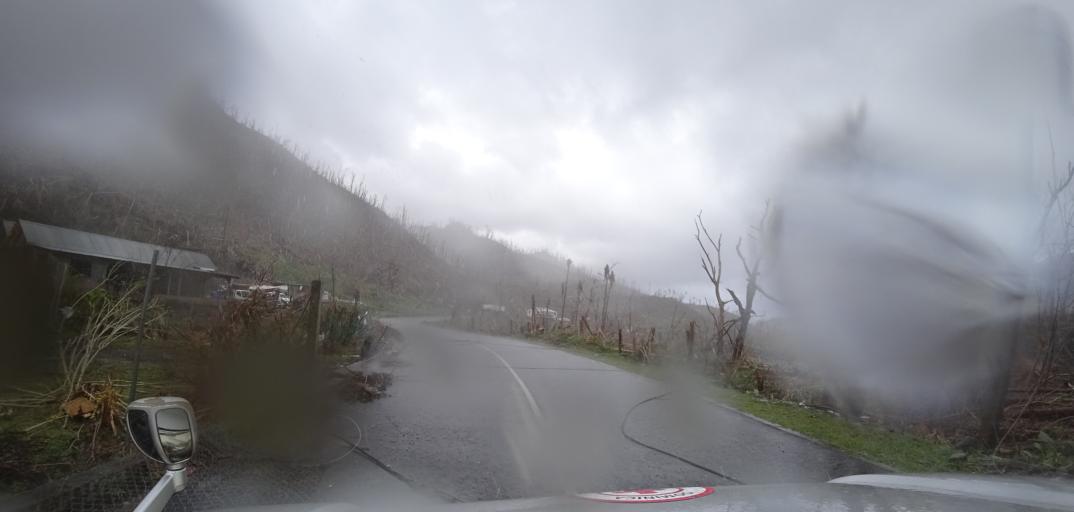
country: DM
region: Saint Andrew
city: Marigot
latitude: 15.4883
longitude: -61.2773
